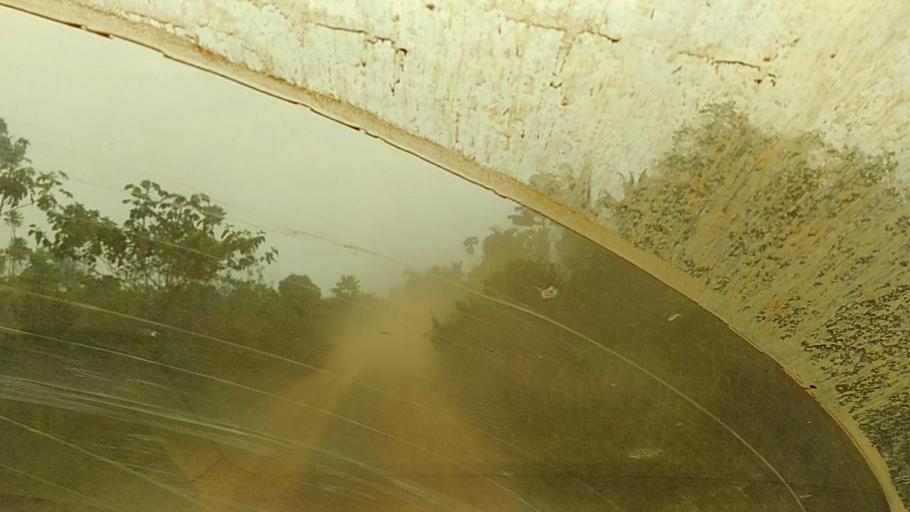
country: BR
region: Rondonia
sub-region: Porto Velho
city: Porto Velho
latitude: -8.7730
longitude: -63.1990
